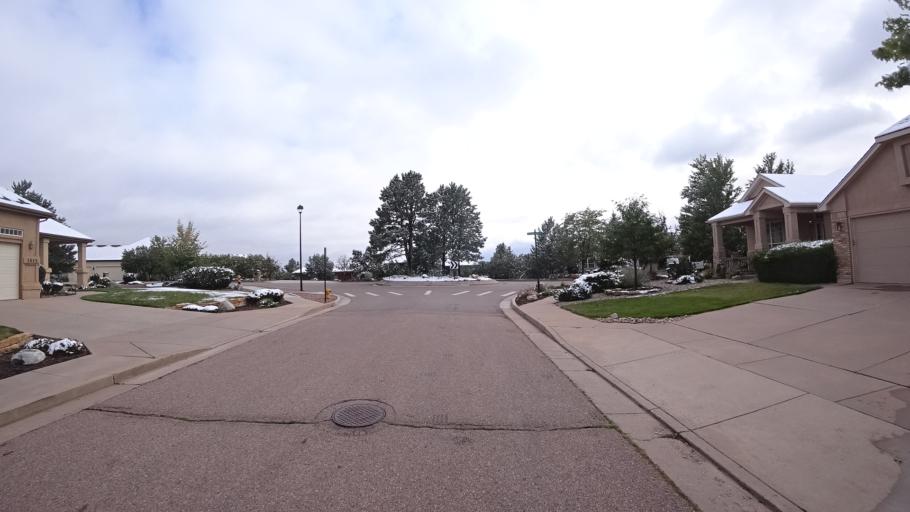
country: US
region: Colorado
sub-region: El Paso County
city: Colorado Springs
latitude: 38.9126
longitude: -104.7977
